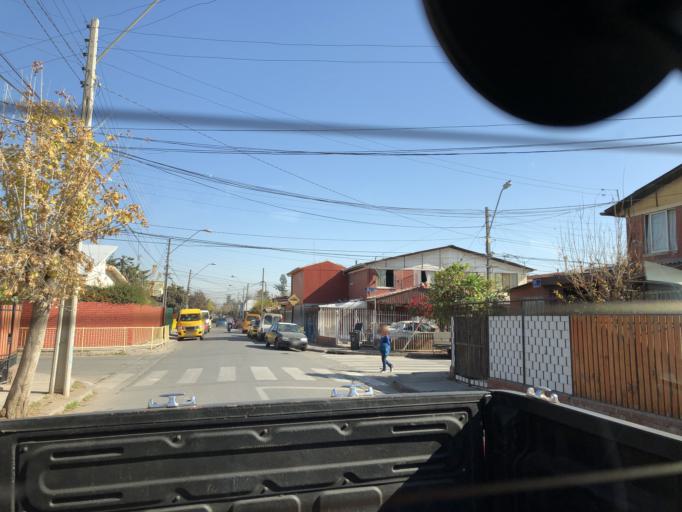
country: CL
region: Santiago Metropolitan
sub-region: Provincia de Cordillera
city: Puente Alto
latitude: -33.5649
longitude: -70.5732
